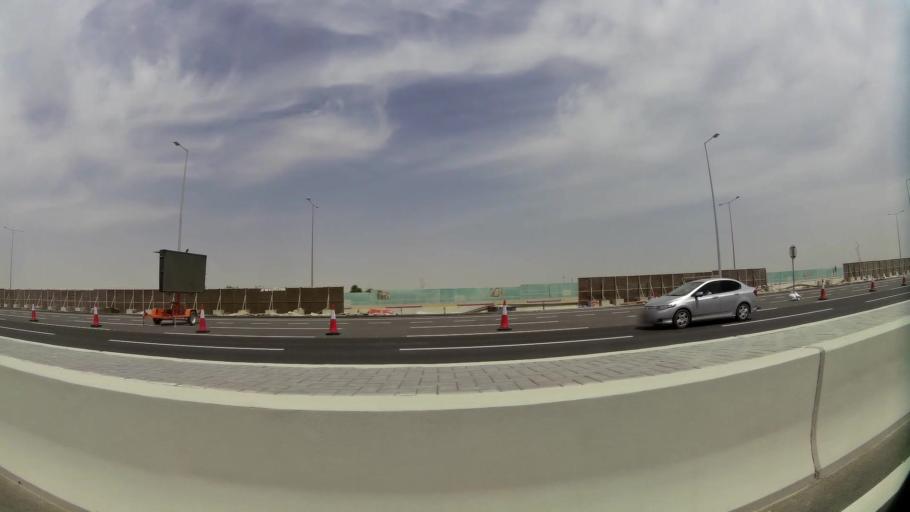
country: QA
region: Baladiyat ar Rayyan
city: Ar Rayyan
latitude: 25.3048
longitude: 51.4164
